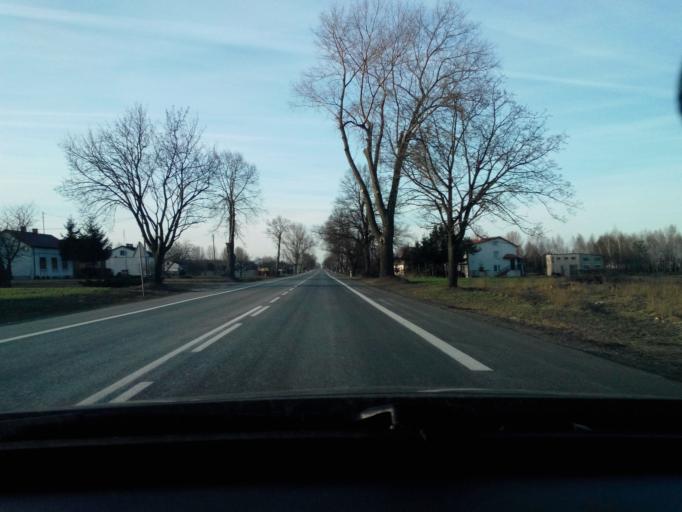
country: PL
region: Kujawsko-Pomorskie
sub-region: Powiat wloclawski
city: Lubien Kujawski
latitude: 52.4127
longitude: 19.1666
